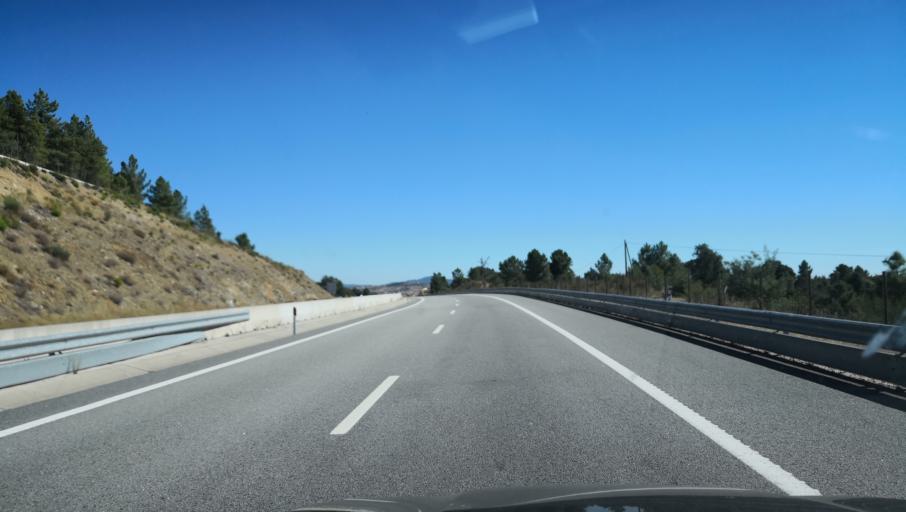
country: PT
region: Vila Real
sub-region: Murca
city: Murca
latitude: 41.4260
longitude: -7.3902
